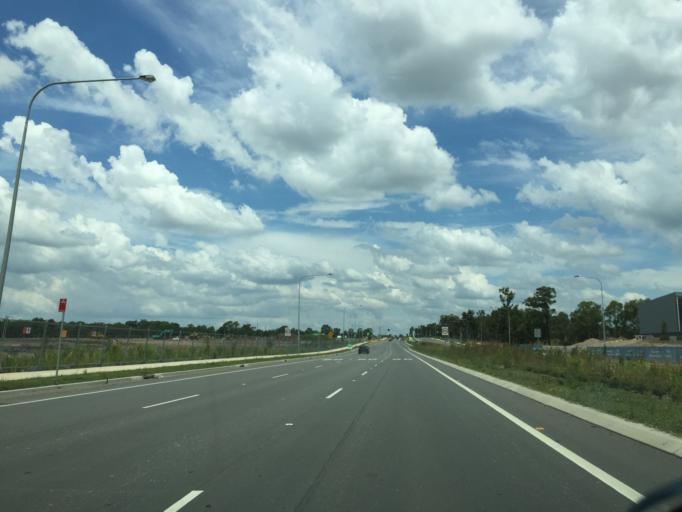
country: AU
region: New South Wales
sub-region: Blacktown
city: Hassall Grove
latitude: -33.7207
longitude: 150.8443
